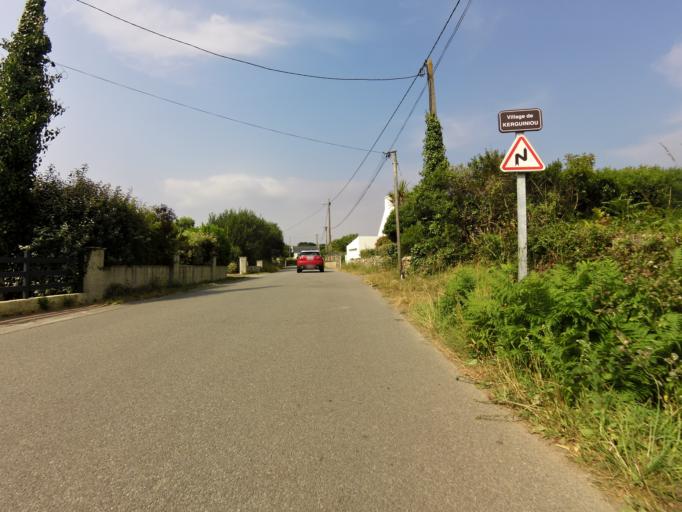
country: FR
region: Brittany
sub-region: Departement du Finistere
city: Esquibien
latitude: 48.0153
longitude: -4.5651
